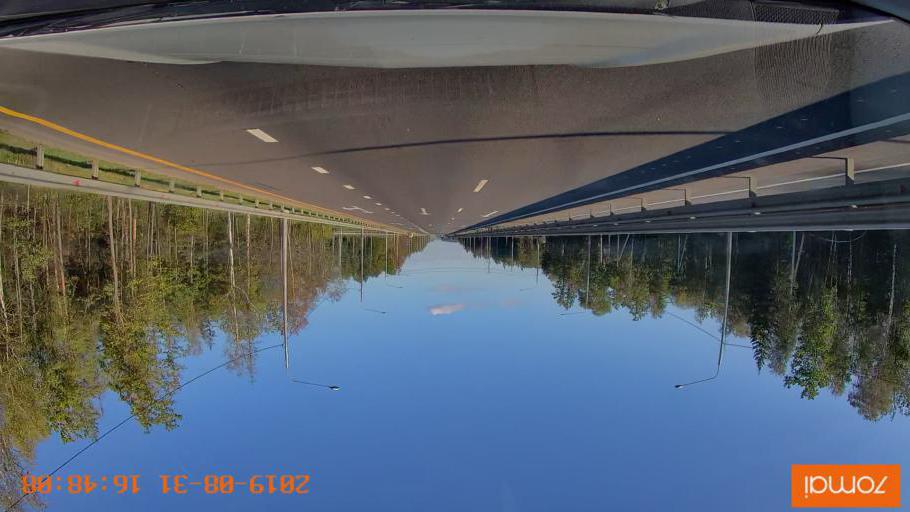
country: RU
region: Kaluga
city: Pyatovskiy
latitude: 54.6667
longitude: 36.1444
